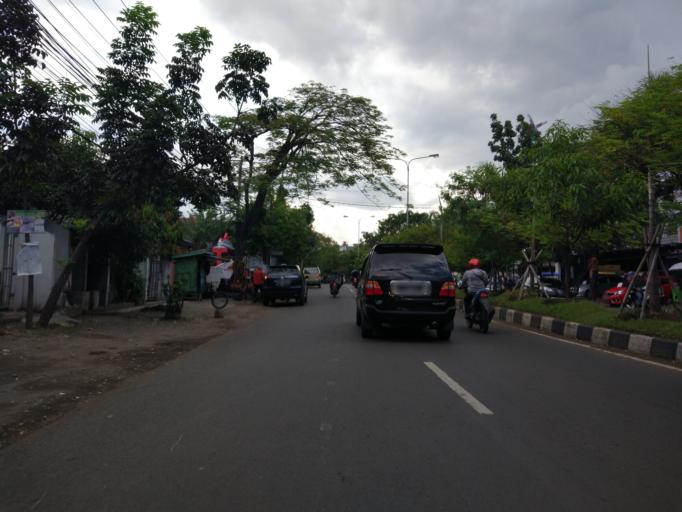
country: ID
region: West Java
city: Bandung
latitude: -6.9125
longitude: 107.6546
